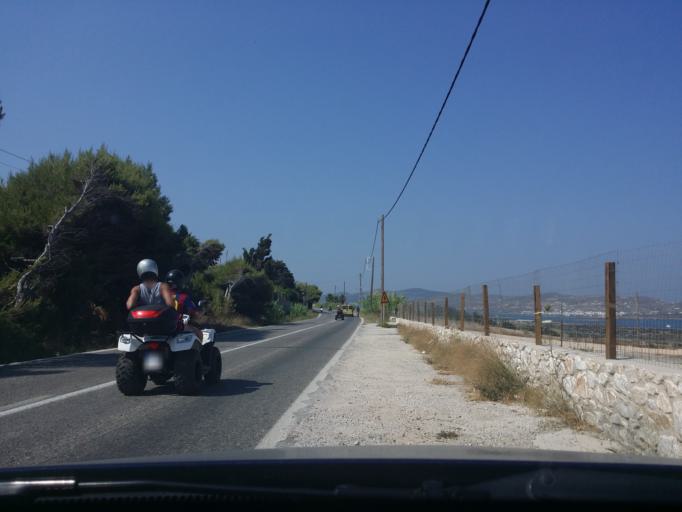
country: GR
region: South Aegean
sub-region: Nomos Kykladon
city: Paros
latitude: 37.0600
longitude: 25.1187
